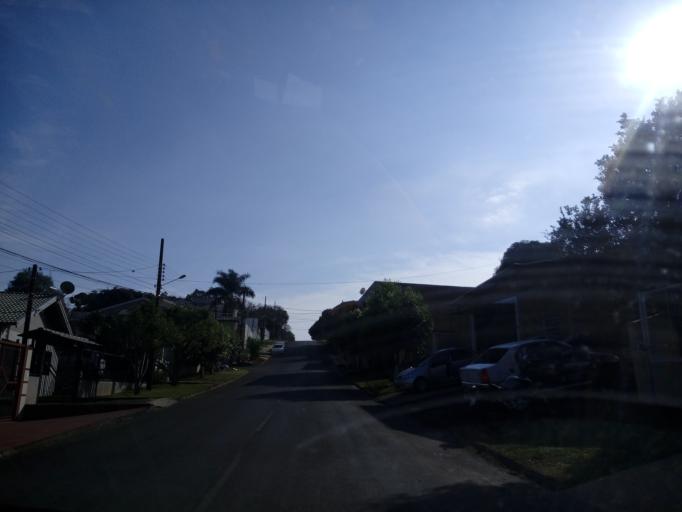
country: BR
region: Santa Catarina
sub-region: Chapeco
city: Chapeco
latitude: -27.1232
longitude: -52.6148
